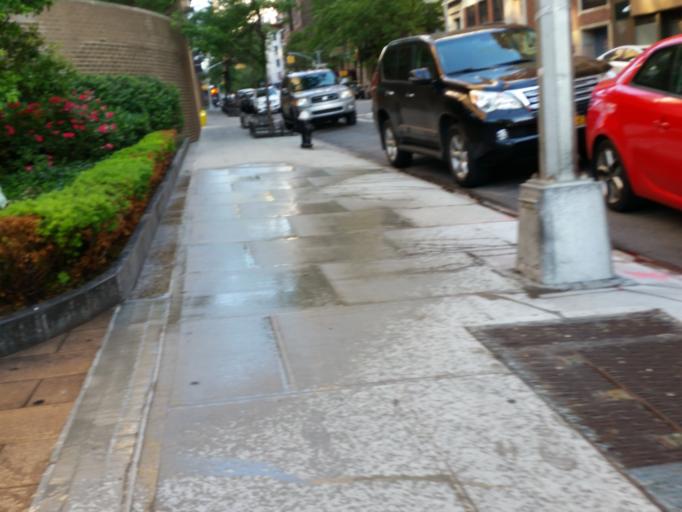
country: US
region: New York
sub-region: Queens County
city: Long Island City
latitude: 40.7465
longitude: -73.9722
